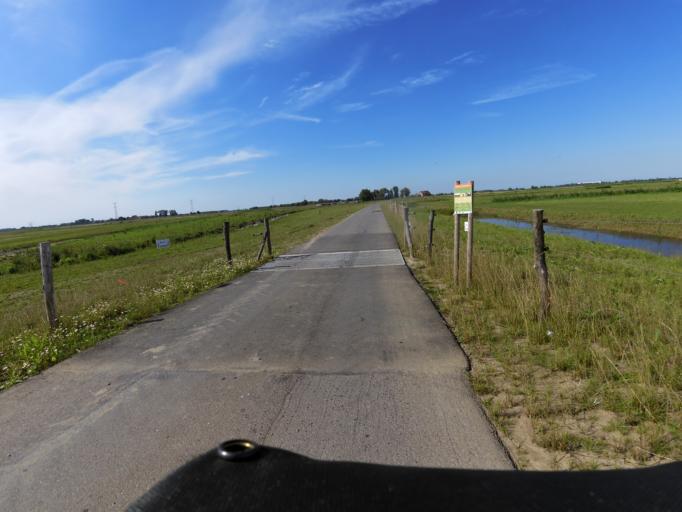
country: NL
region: South Holland
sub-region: Gemeente Hardinxveld-Giessendam
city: Neder-Hardinxveld
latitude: 51.7847
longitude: 4.8438
